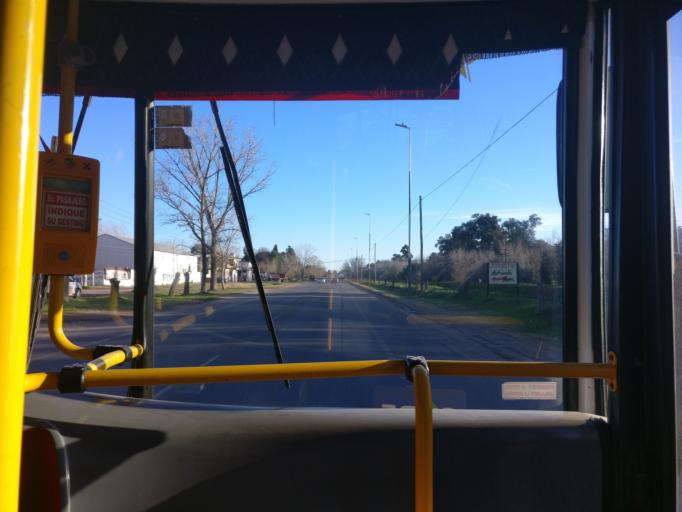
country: AR
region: Buenos Aires
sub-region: Partido de Ezeiza
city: Ezeiza
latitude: -34.9120
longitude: -58.5965
